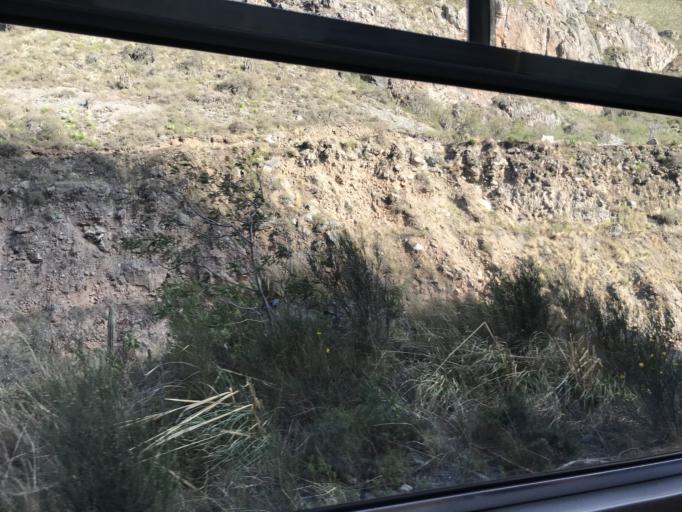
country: PE
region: Cusco
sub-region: Provincia de Urubamba
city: Ollantaytambo
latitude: -13.2165
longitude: -72.3854
